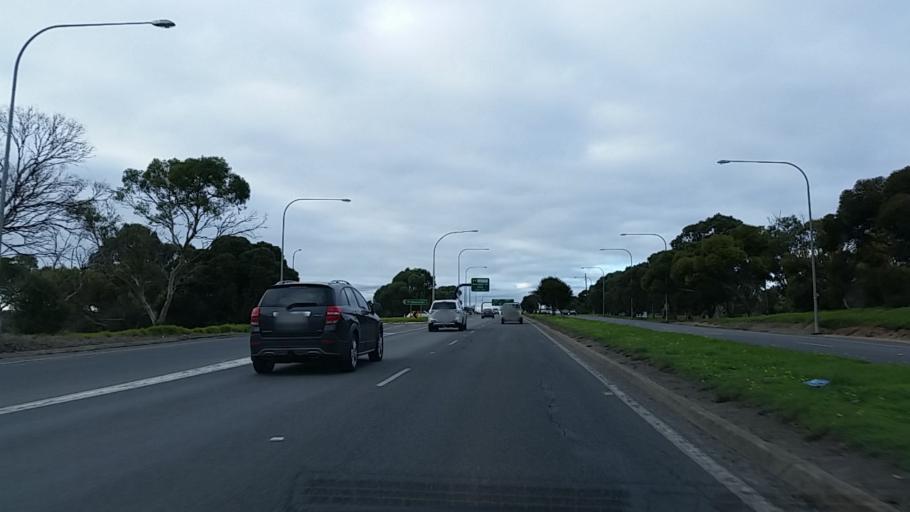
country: AU
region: South Australia
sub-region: Onkaparinga
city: Noarlunga
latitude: -35.1702
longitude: 138.5032
